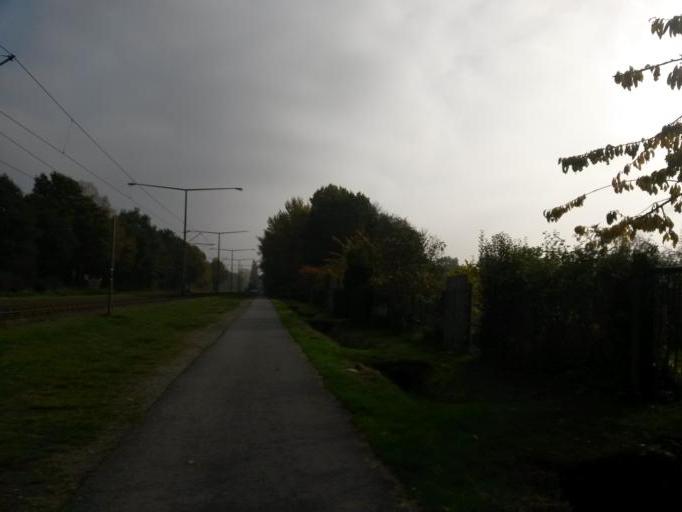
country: DE
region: Bremen
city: Bremen
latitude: 53.0769
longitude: 8.8645
